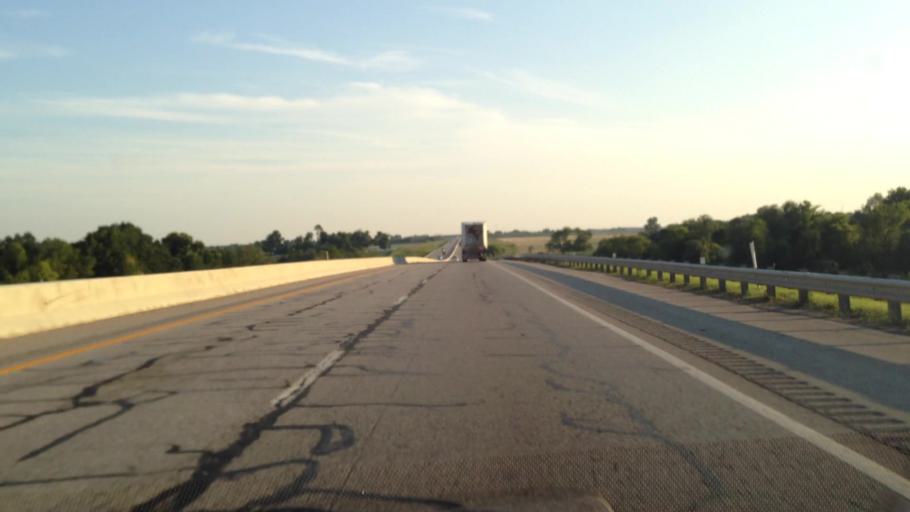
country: US
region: Oklahoma
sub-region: Ottawa County
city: Miami
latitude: 36.8135
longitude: -94.8745
